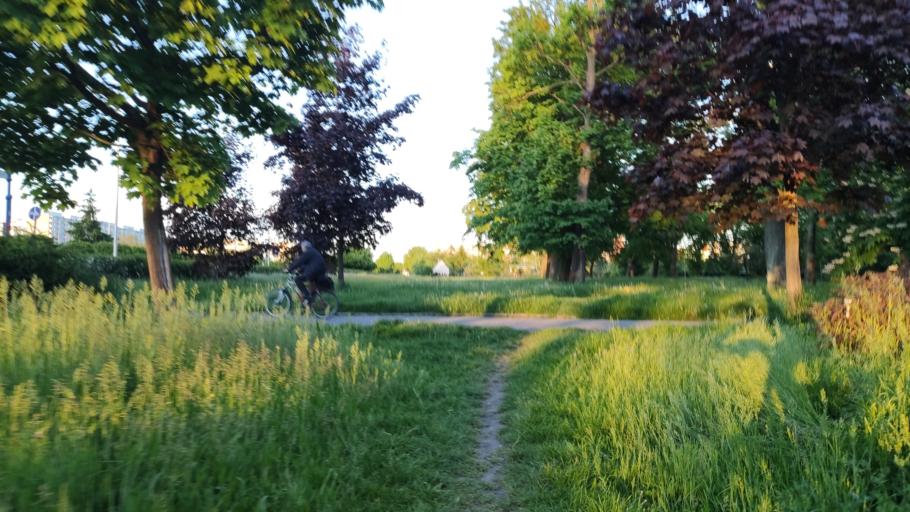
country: PL
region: Lower Silesian Voivodeship
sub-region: Powiat wroclawski
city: Wroclaw
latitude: 51.0830
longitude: 17.0302
